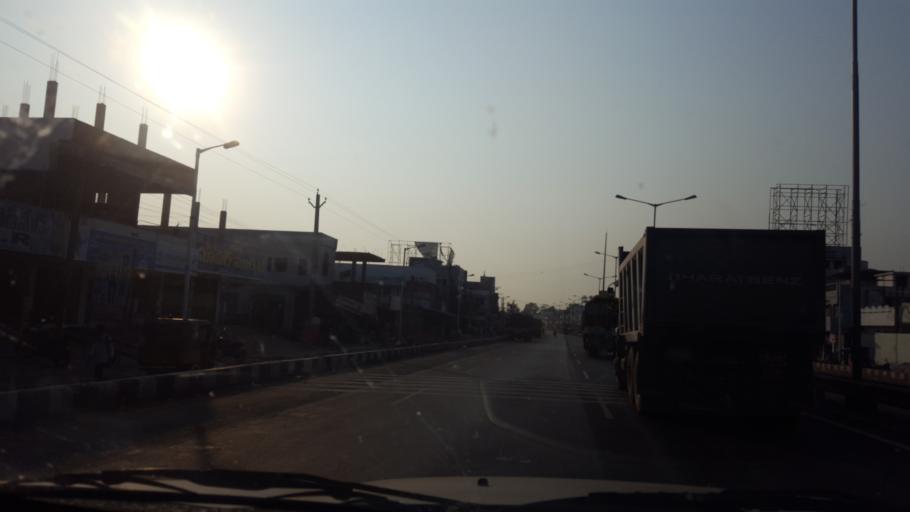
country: IN
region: Andhra Pradesh
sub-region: East Godavari
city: Pithapuram
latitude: 17.2426
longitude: 82.3375
